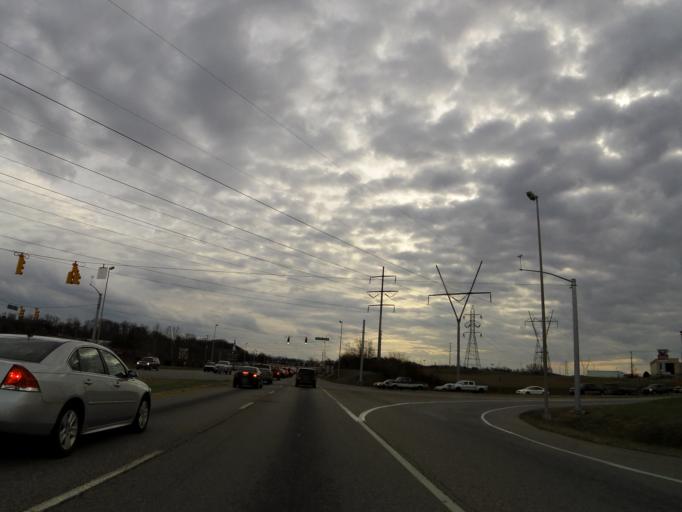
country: US
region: Tennessee
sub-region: Blount County
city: Maryville
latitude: 35.7531
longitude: -83.9944
